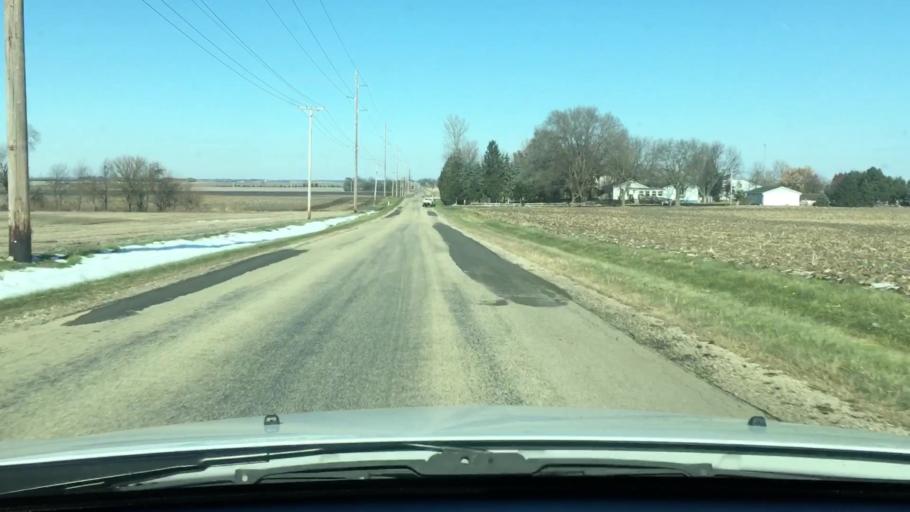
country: US
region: Illinois
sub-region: Ogle County
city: Hillcrest
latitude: 41.9405
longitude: -89.0004
